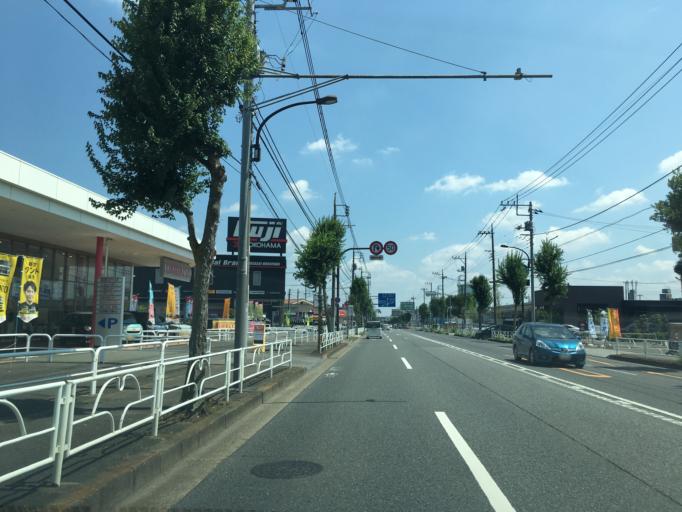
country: JP
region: Tokyo
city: Fussa
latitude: 35.7515
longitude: 139.3868
